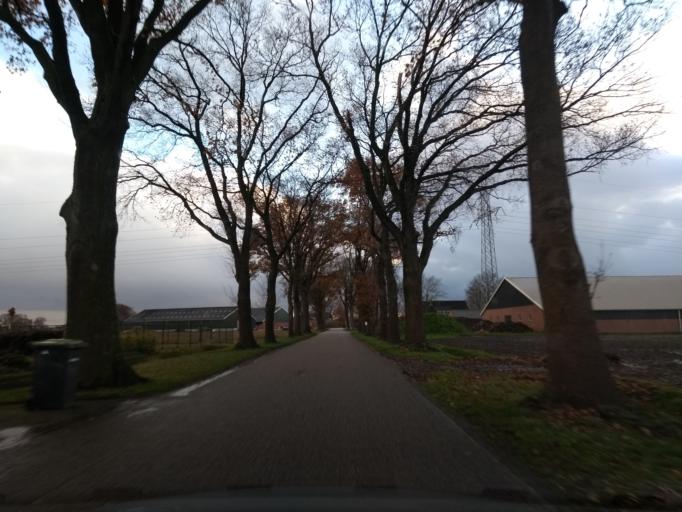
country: NL
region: Overijssel
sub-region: Gemeente Almelo
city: Almelo
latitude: 52.3946
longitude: 6.6904
